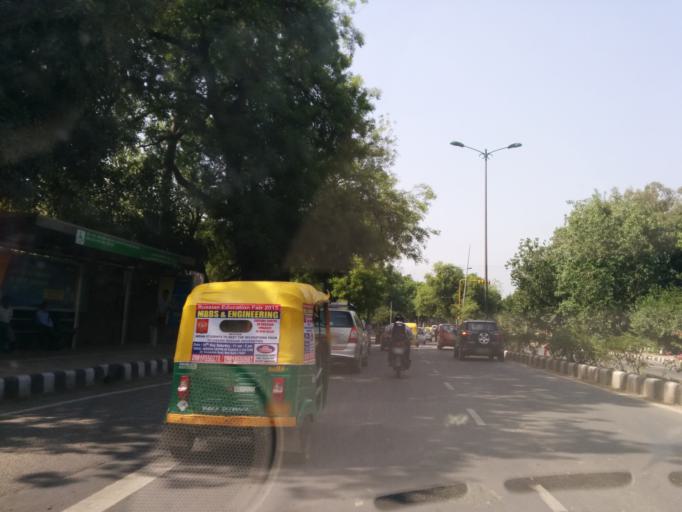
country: IN
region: NCT
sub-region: New Delhi
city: New Delhi
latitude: 28.5402
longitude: 77.1994
